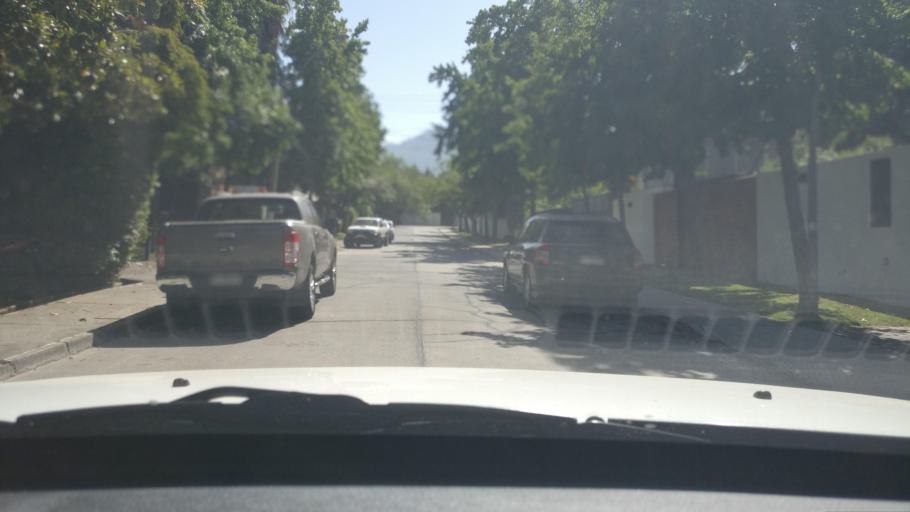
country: CL
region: Santiago Metropolitan
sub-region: Provincia de Santiago
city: Villa Presidente Frei, Nunoa, Santiago, Chile
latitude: -33.3748
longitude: -70.5121
